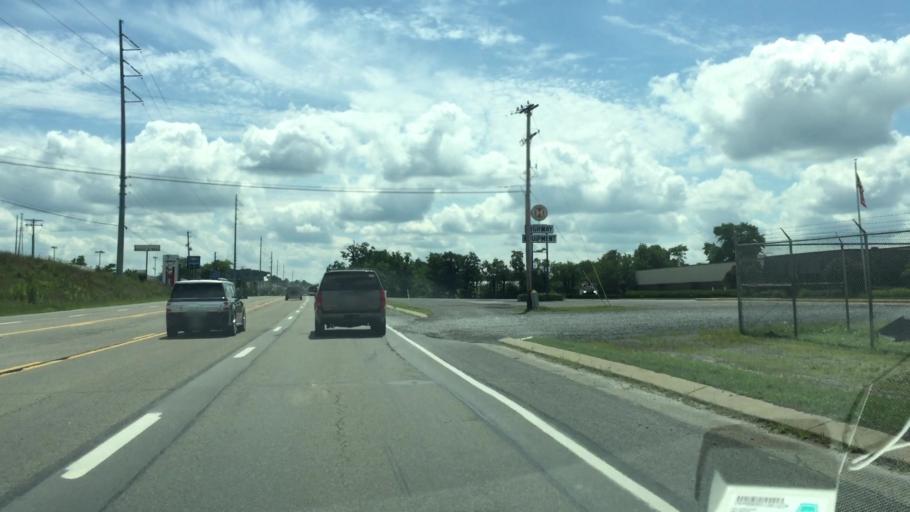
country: US
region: Pennsylvania
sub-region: Butler County
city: Zelienople
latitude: 40.7484
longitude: -80.1152
